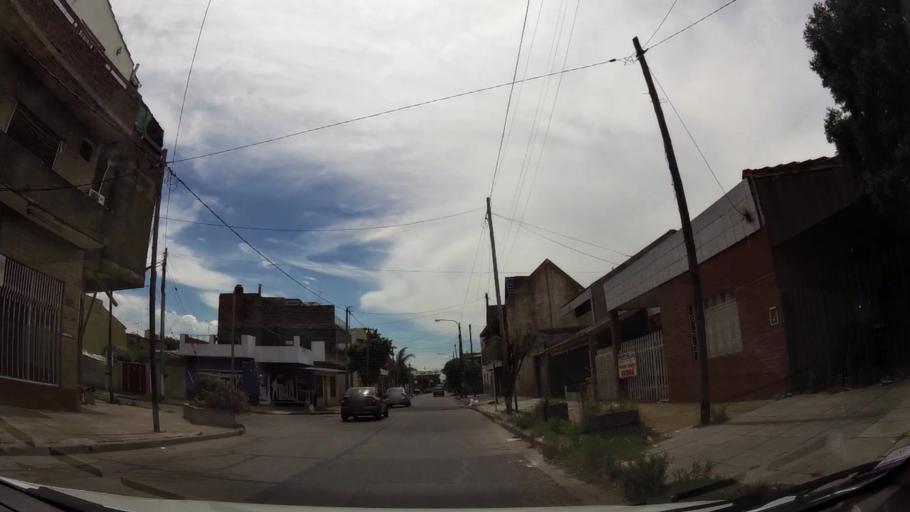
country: AR
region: Buenos Aires
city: San Justo
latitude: -34.6820
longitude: -58.5366
